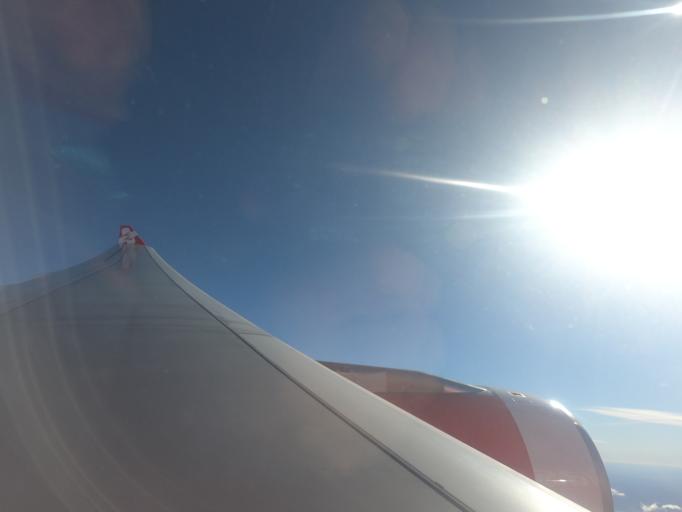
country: AU
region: New South Wales
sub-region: Wollondilly
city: Oakdale
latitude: -34.1481
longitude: 150.1540
